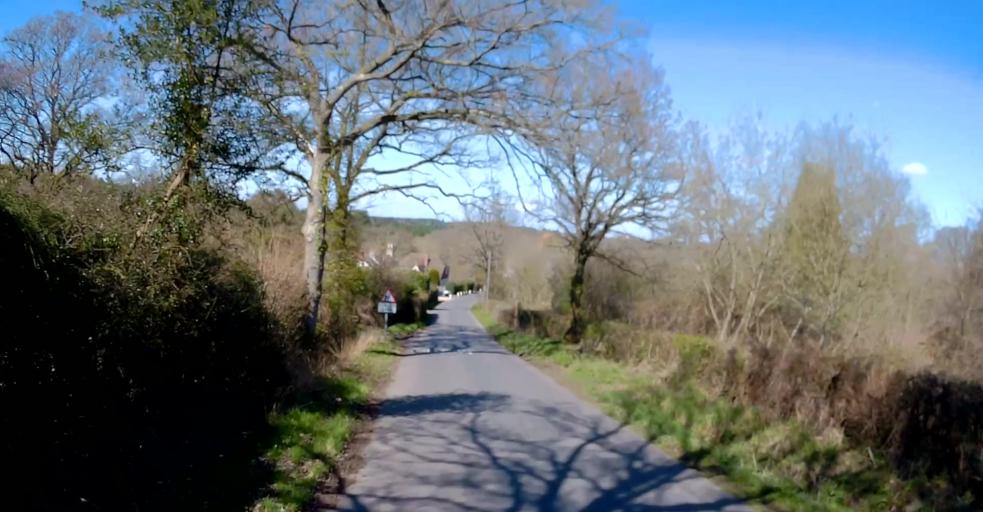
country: GB
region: England
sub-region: Hampshire
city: Lindford
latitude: 51.1638
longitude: -0.8288
